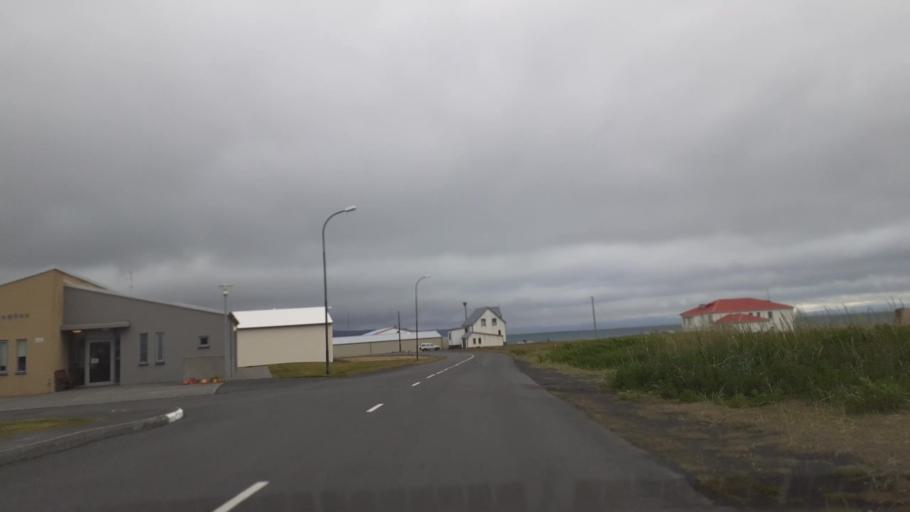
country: IS
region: Northeast
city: Husavik
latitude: 66.3017
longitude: -16.4486
